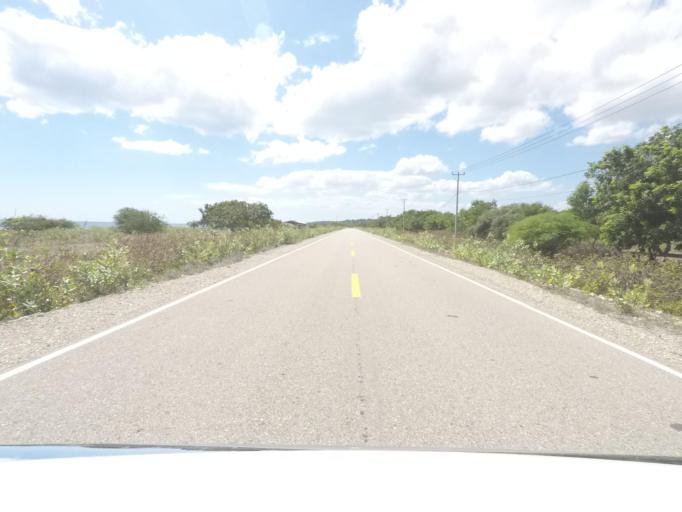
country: TL
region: Baucau
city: Baucau
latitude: -8.4215
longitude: 126.7053
